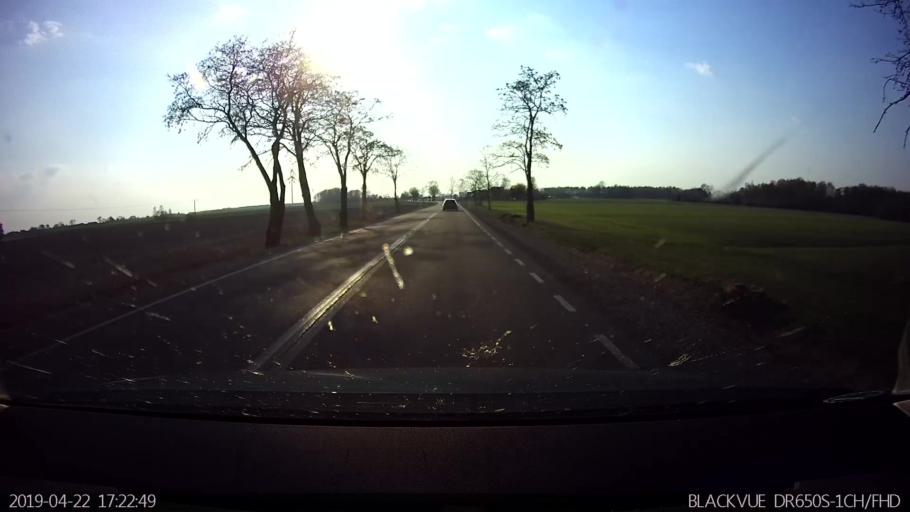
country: PL
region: Masovian Voivodeship
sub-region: Powiat sokolowski
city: Repki
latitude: 52.3894
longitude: 22.3310
